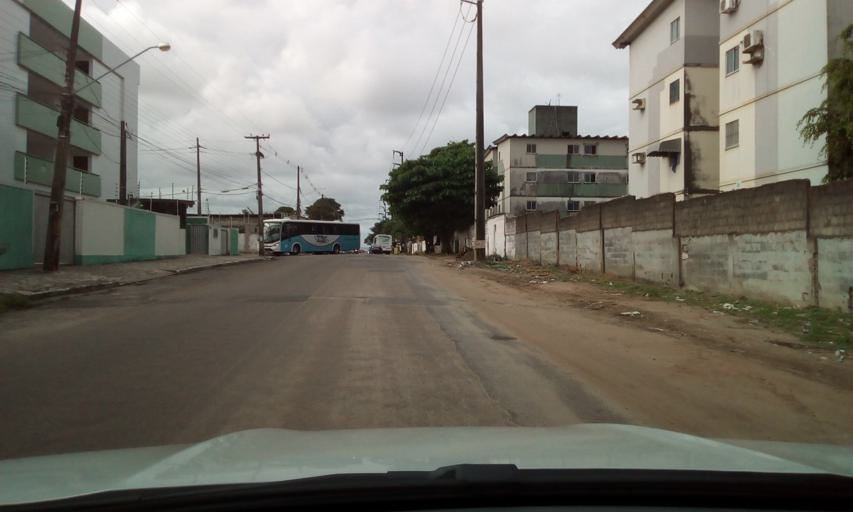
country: BR
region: Paraiba
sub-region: Joao Pessoa
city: Joao Pessoa
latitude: -7.1849
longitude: -34.8737
